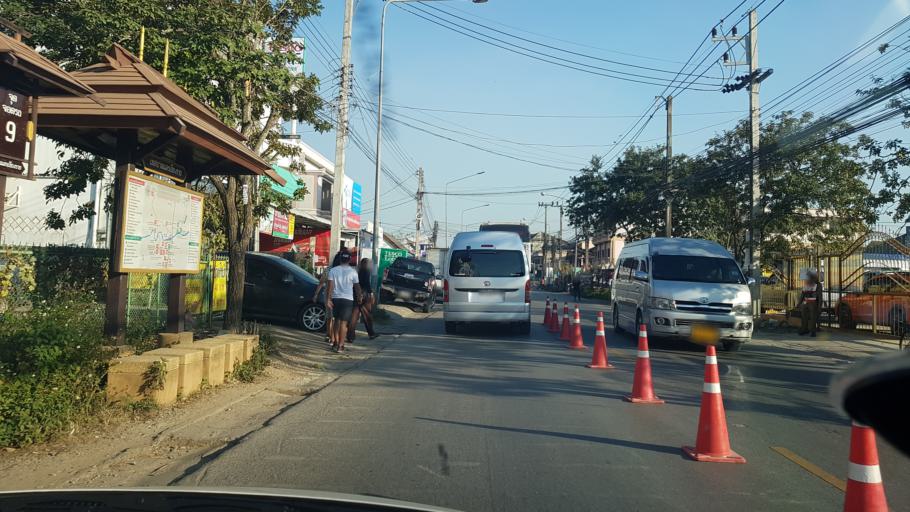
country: TH
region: Chiang Rai
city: Chiang Rai
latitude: 19.9267
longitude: 99.8356
